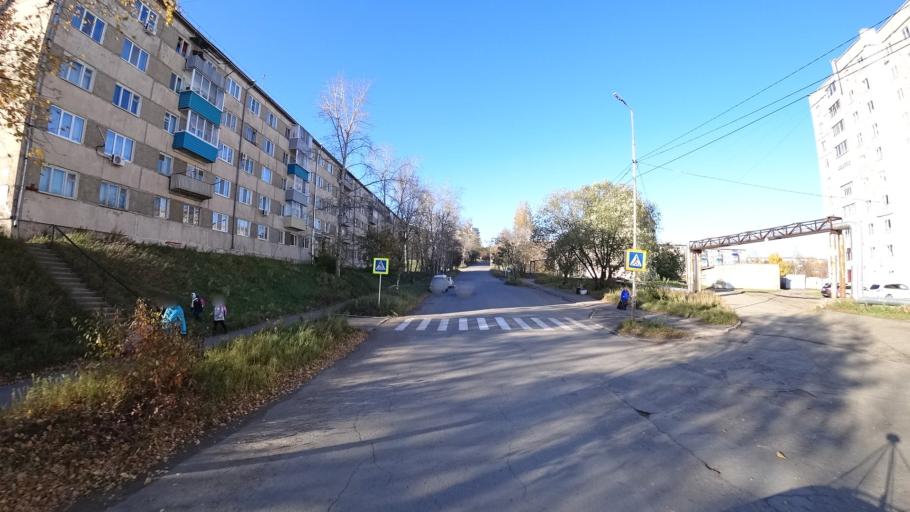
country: RU
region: Khabarovsk Krai
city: Amursk
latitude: 50.2382
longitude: 136.9048
